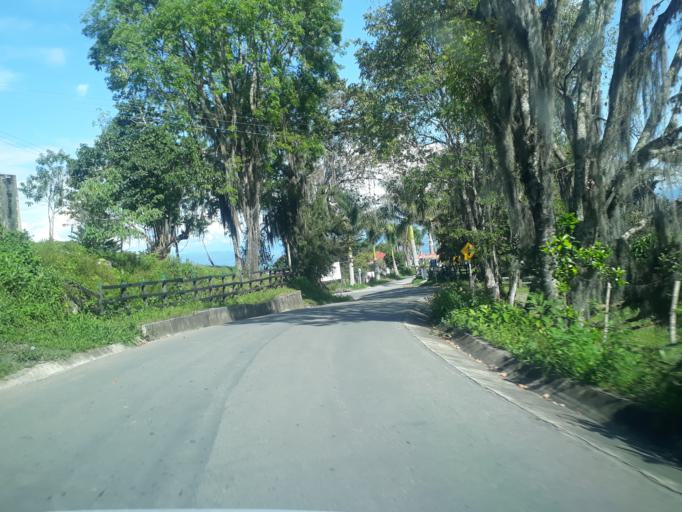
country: CO
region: Santander
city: Velez
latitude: 6.0304
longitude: -73.6544
